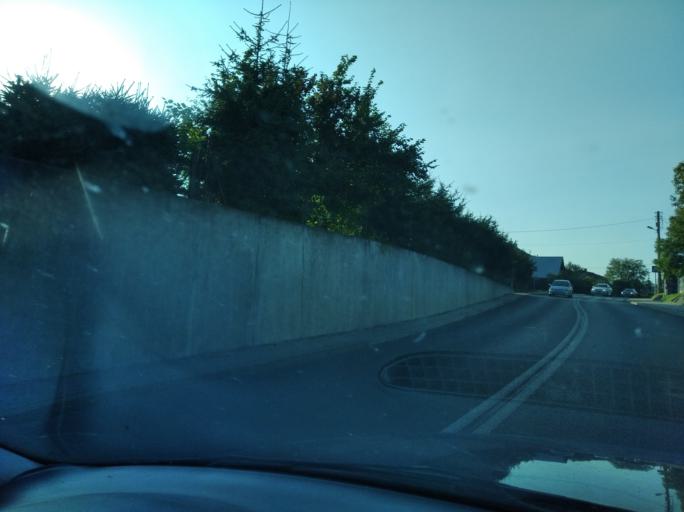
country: PL
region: Subcarpathian Voivodeship
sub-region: Powiat lezajski
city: Stare Miasto
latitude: 50.2830
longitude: 22.4304
